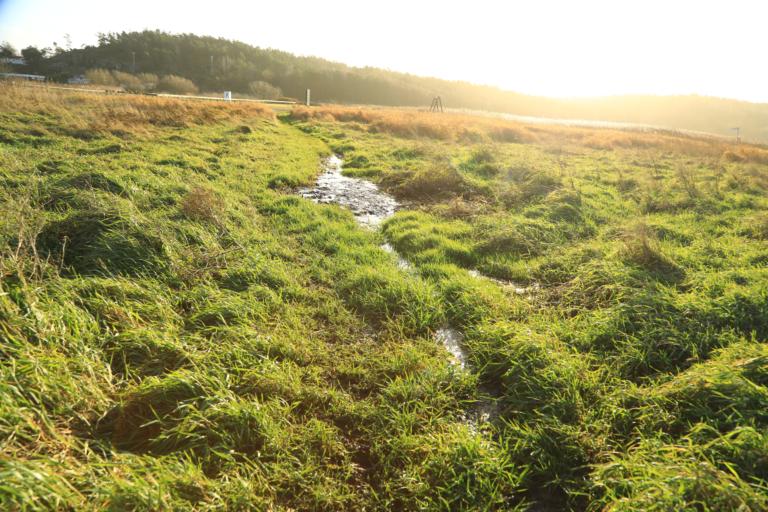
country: SE
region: Halland
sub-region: Varbergs Kommun
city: Varberg
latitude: 57.1824
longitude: 12.2141
